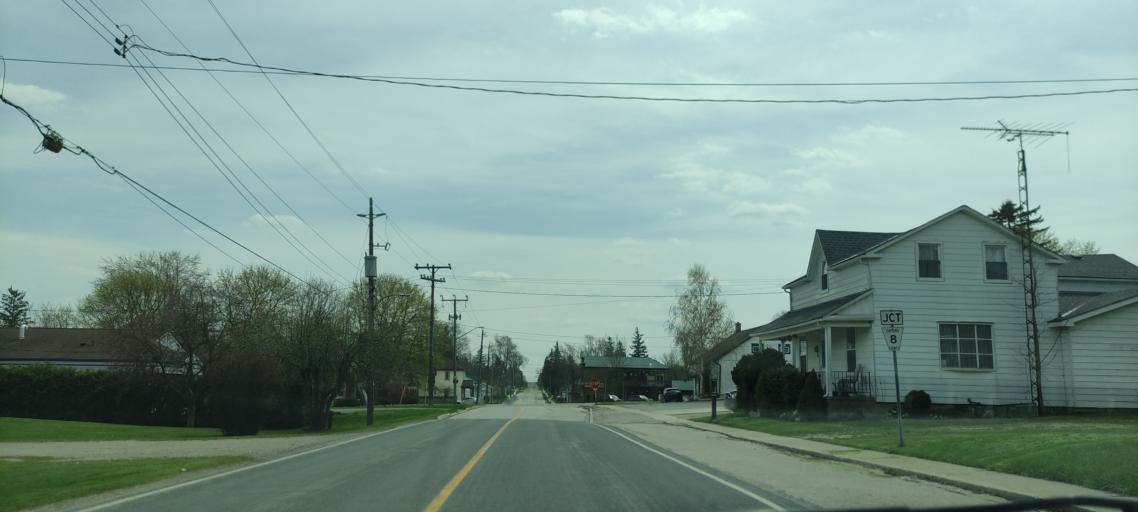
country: CA
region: Ontario
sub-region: Oxford County
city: Woodstock
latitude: 43.2725
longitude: -80.6583
